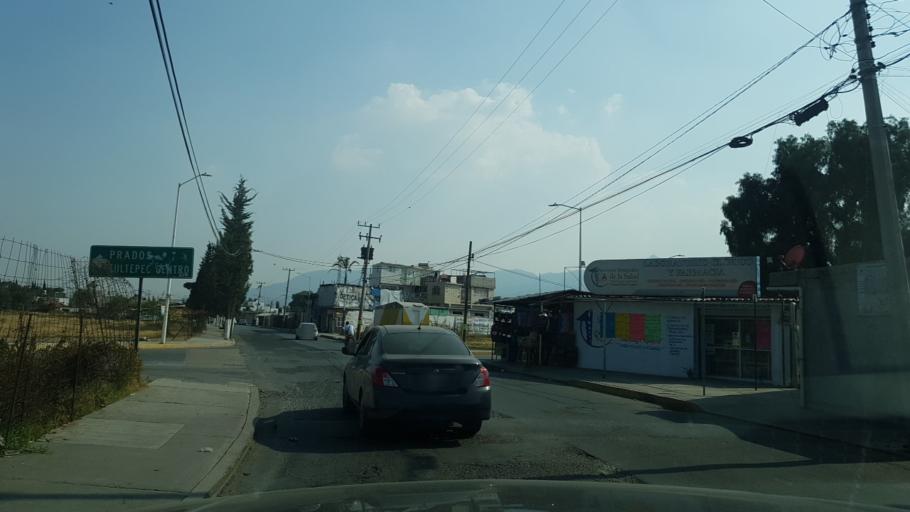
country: MX
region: Mexico
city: Santiago Teyahualco
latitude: 19.6598
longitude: -99.1276
